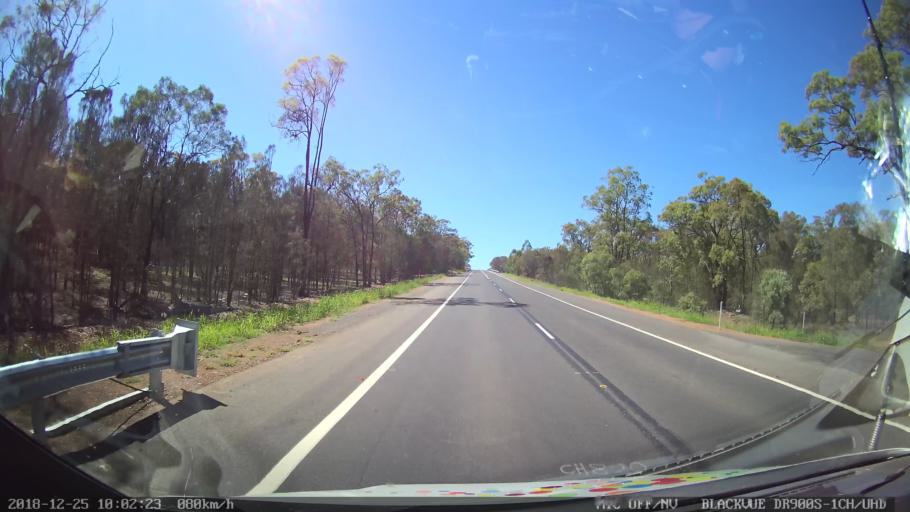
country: AU
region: New South Wales
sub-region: Upper Hunter Shire
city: Merriwa
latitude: -32.2179
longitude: 150.4634
